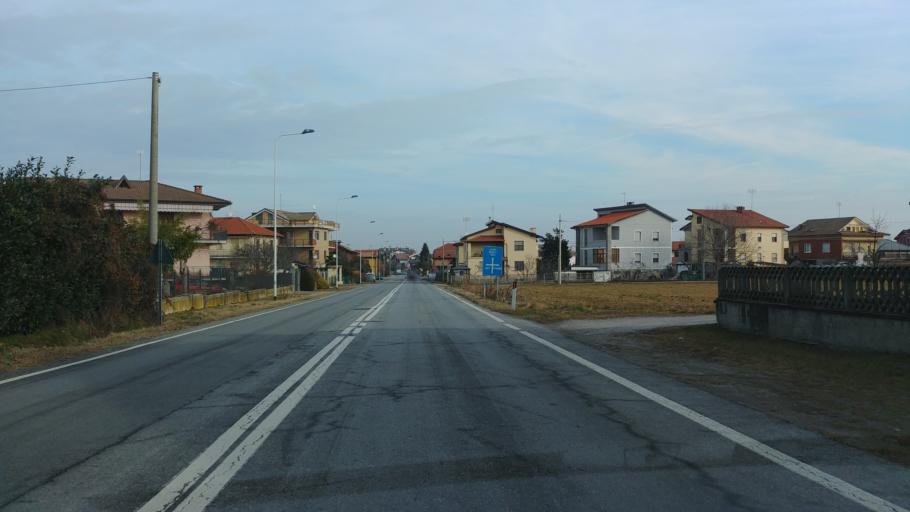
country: IT
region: Piedmont
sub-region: Provincia di Cuneo
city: Cuneo
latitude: 44.3839
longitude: 7.5617
